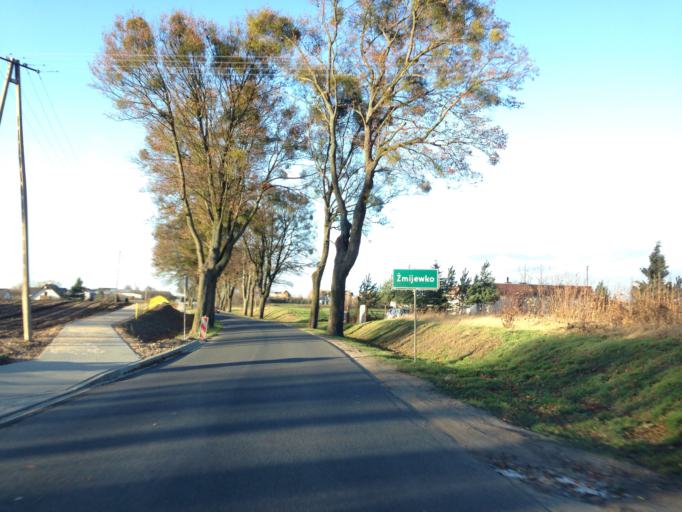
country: PL
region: Kujawsko-Pomorskie
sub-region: Powiat brodnicki
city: Brodnica
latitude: 53.3034
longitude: 19.3974
